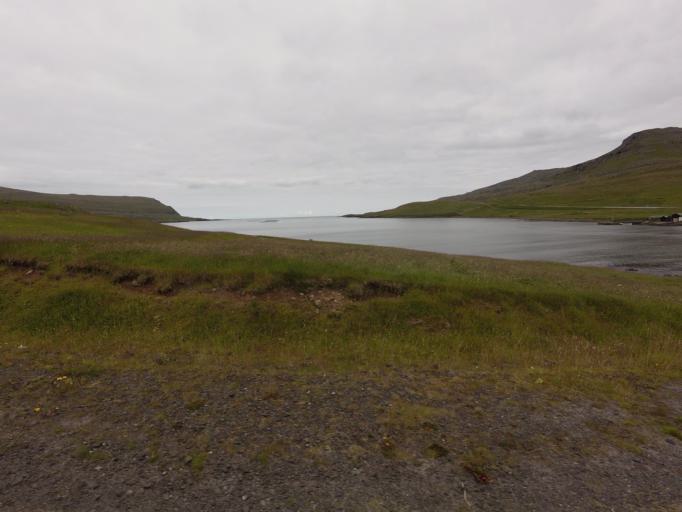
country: FO
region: Suduroy
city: Tvoroyri
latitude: 61.5356
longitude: -6.8120
